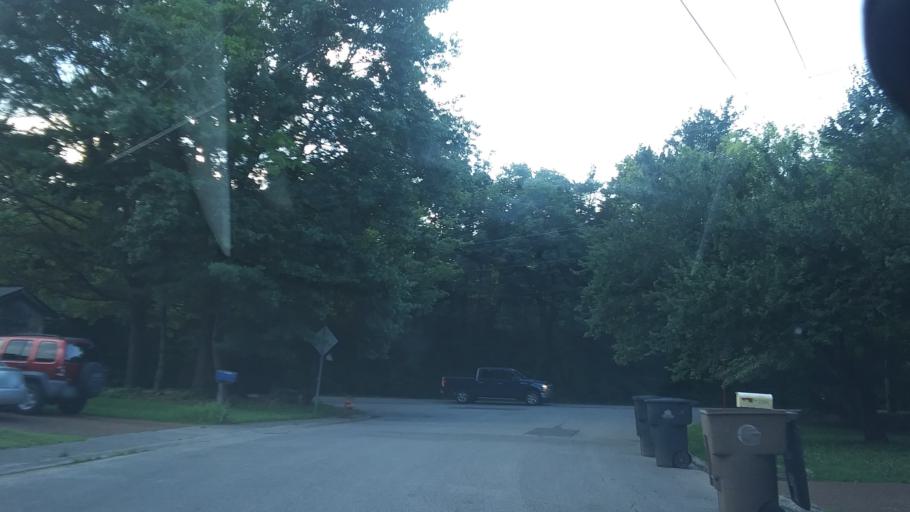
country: US
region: Tennessee
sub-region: Rutherford County
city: La Vergne
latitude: 36.0790
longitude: -86.6686
